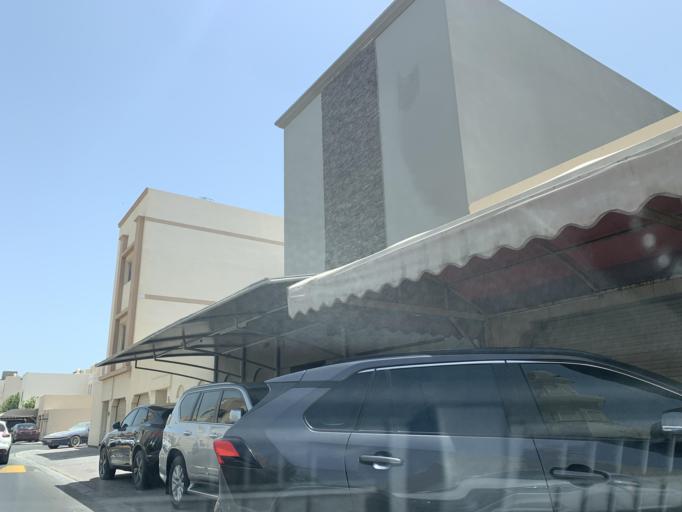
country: BH
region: Northern
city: Sitrah
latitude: 26.1401
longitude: 50.5929
